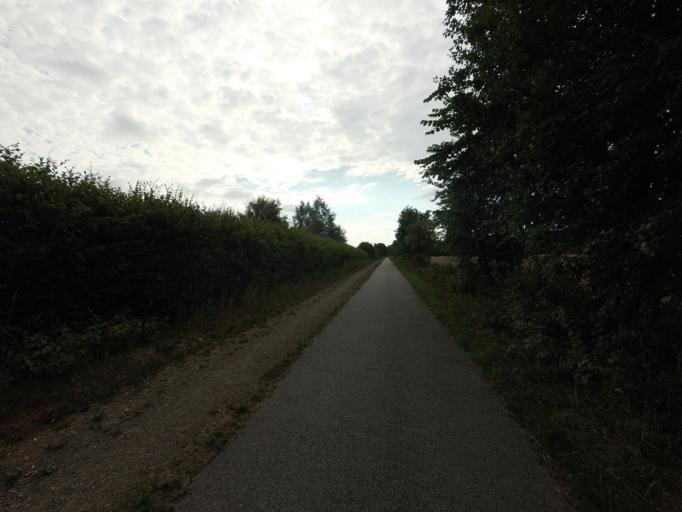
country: SE
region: Skane
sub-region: Helsingborg
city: Odakra
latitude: 56.1745
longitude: 12.6913
